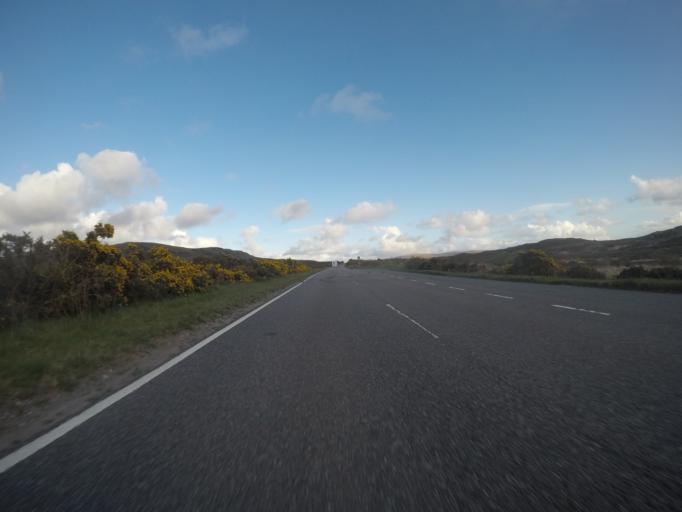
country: GB
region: Scotland
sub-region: Highland
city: Portree
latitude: 57.4724
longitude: -6.2953
